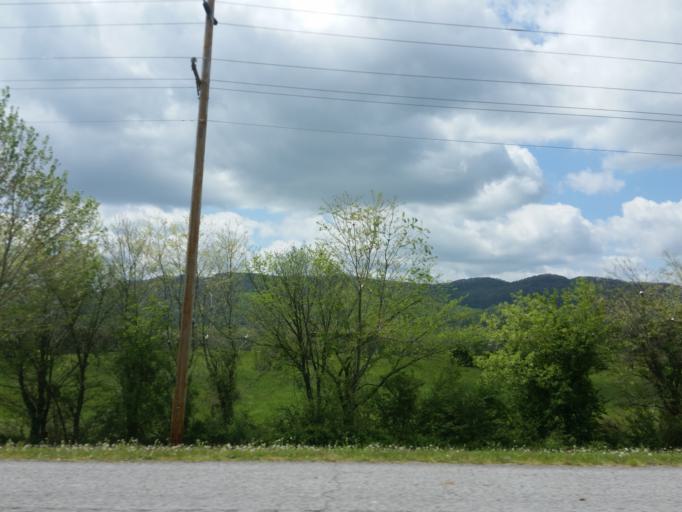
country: US
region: Tennessee
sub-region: Claiborne County
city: Harrogate
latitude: 36.5541
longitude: -83.6619
